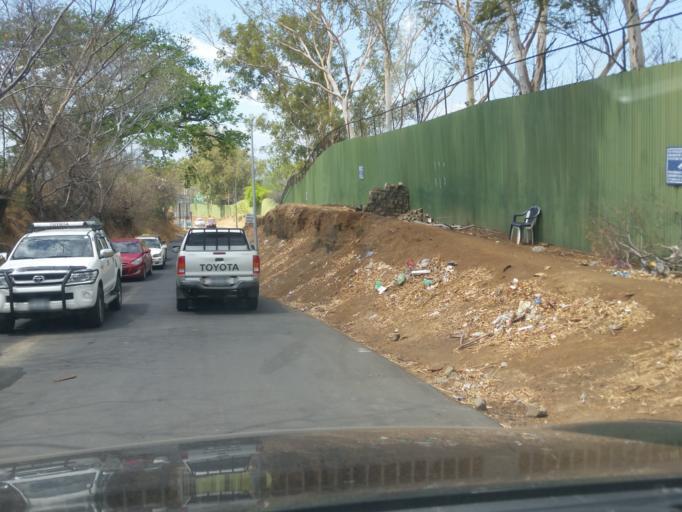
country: NI
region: Managua
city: Managua
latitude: 12.1095
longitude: -86.2792
